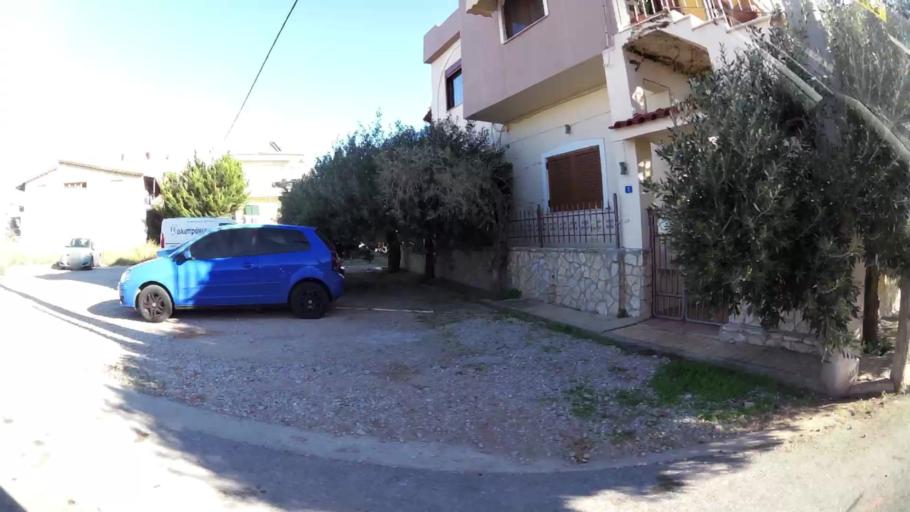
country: GR
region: Attica
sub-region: Nomarchia Anatolikis Attikis
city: Acharnes
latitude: 38.0924
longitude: 23.7350
